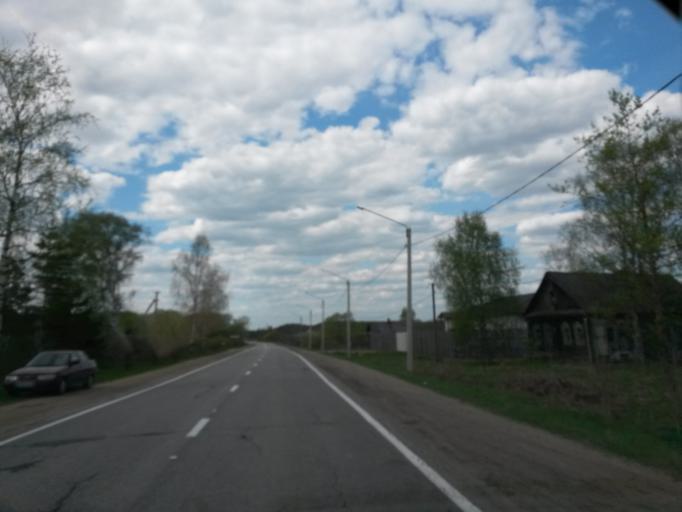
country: RU
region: Jaroslavl
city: Kurba
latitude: 57.6788
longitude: 39.5727
